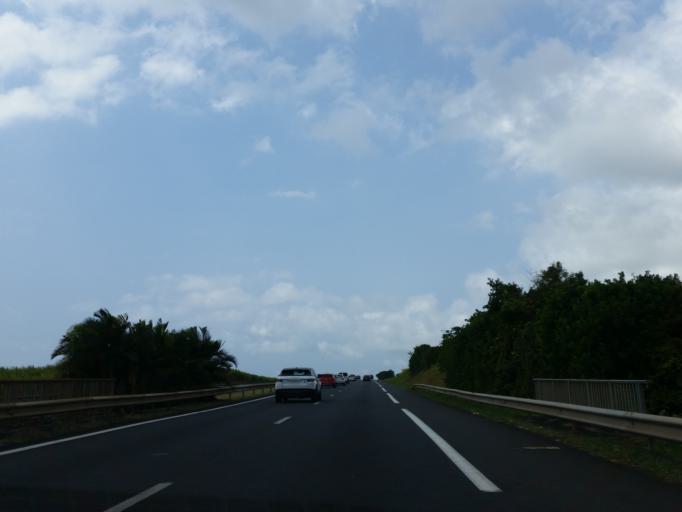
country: RE
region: Reunion
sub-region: Reunion
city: Sainte-Suzanne
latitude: -20.9004
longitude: 55.5864
